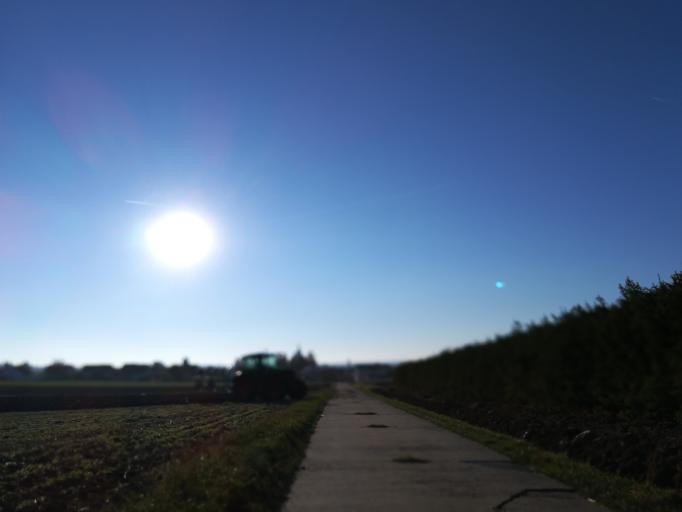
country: DE
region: Baden-Wuerttemberg
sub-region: Regierungsbezirk Stuttgart
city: Neuhausen auf den Fildern
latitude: 48.6843
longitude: 9.2888
